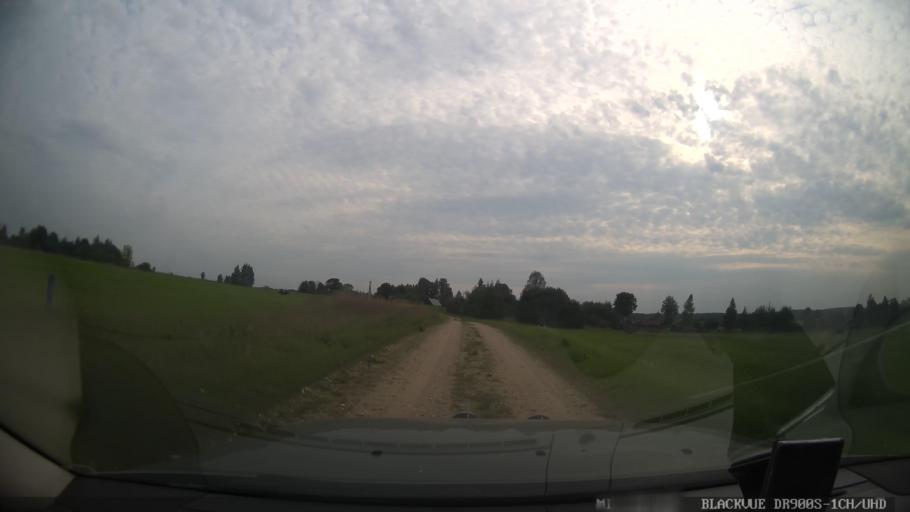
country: BY
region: Grodnenskaya
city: Ashmyany
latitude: 54.5328
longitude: 25.6708
